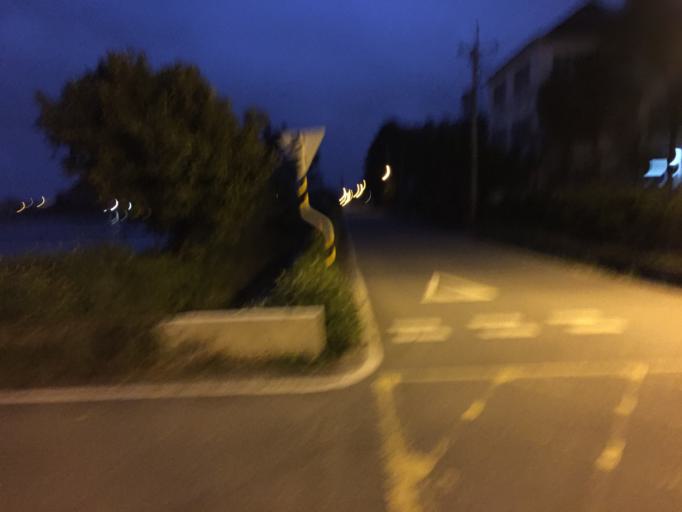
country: TW
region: Taiwan
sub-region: Yilan
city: Yilan
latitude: 24.6561
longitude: 121.7852
